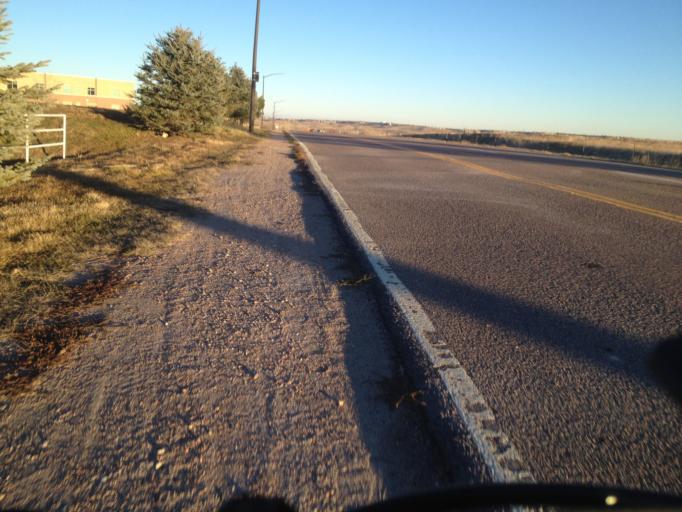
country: US
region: Colorado
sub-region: Boulder County
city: Superior
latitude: 39.9508
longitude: -105.1431
